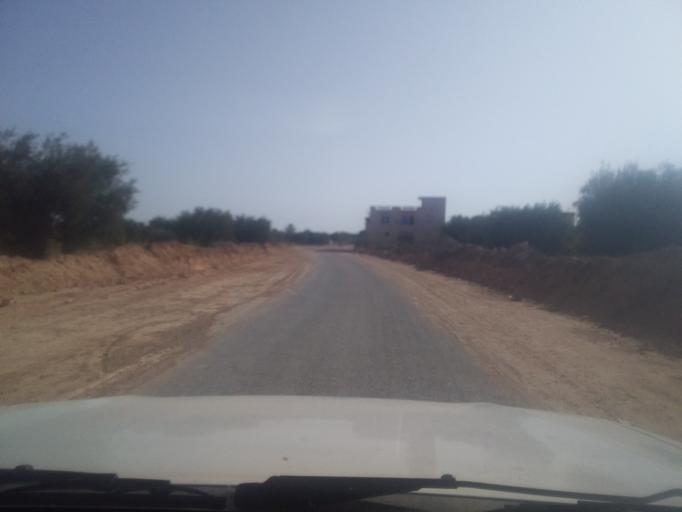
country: TN
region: Qabis
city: Matmata
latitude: 33.6069
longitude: 10.2799
